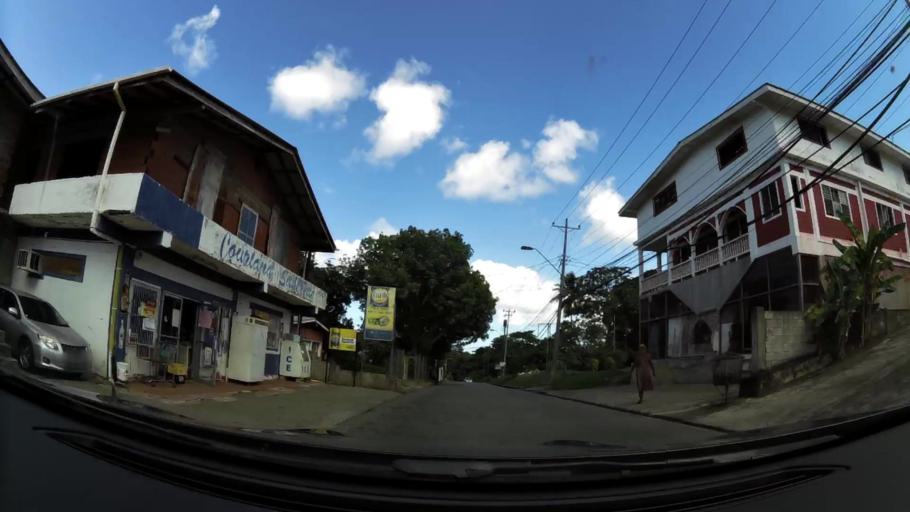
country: TT
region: Tobago
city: Scarborough
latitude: 11.2065
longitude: -60.7803
